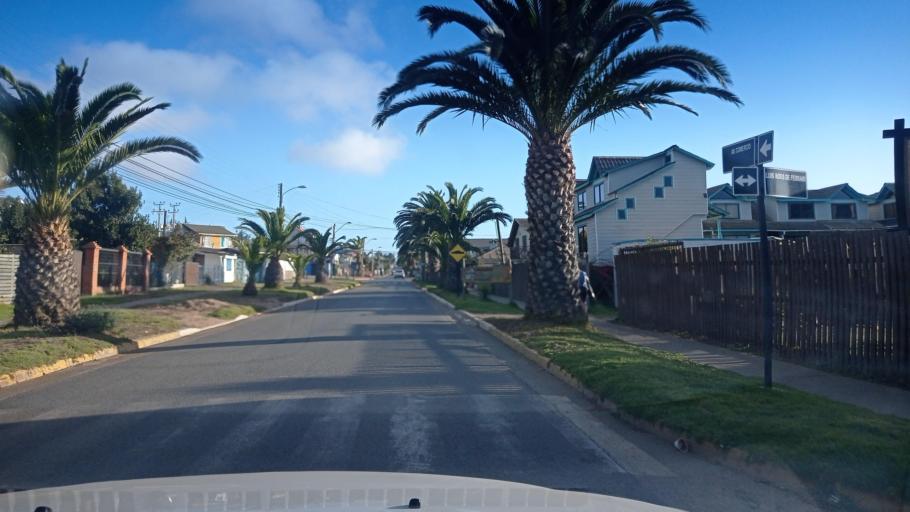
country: CL
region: O'Higgins
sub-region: Provincia de Colchagua
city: Santa Cruz
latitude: -34.3889
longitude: -72.0131
